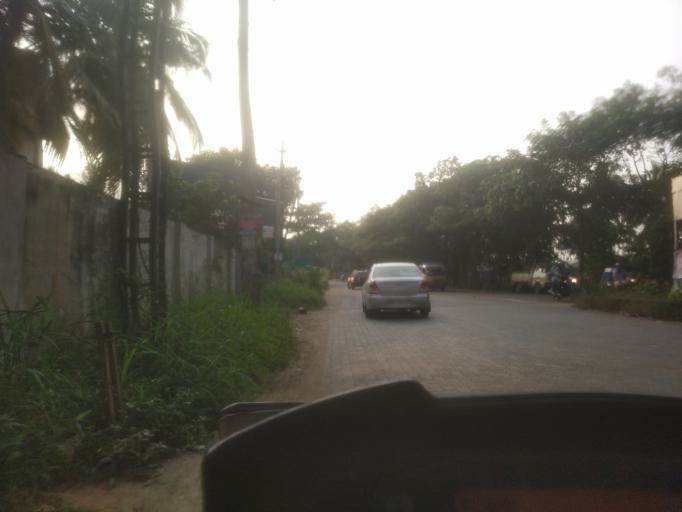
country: IN
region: Kerala
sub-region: Alappuzha
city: Arukutti
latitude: 9.9415
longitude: 76.3395
